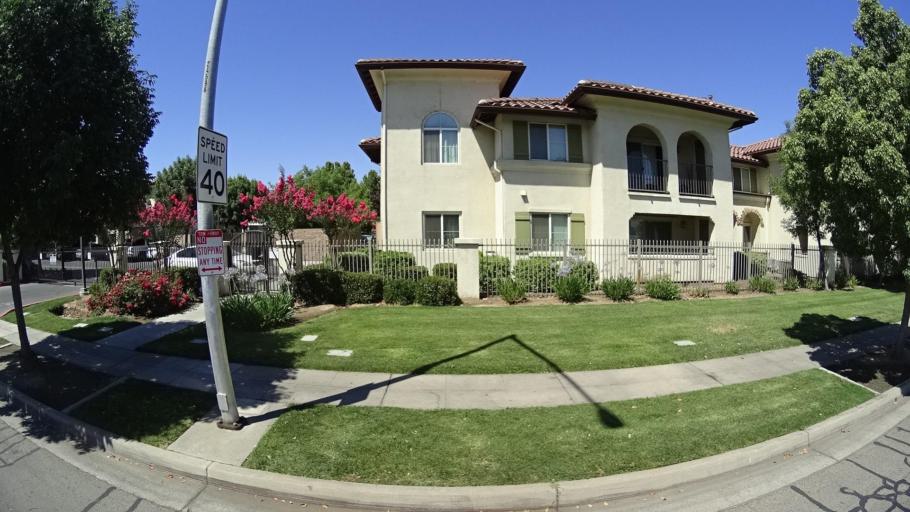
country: US
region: California
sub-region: Fresno County
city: Fresno
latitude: 36.7202
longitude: -119.7912
